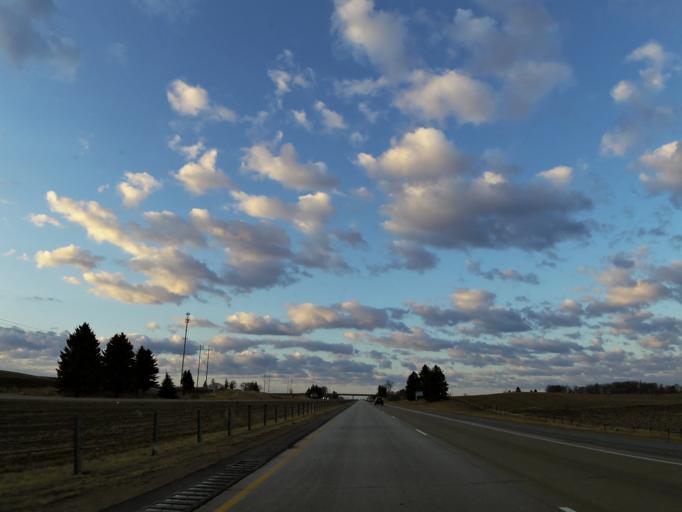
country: US
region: Minnesota
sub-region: Rice County
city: Dundas
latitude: 44.4059
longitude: -93.2927
